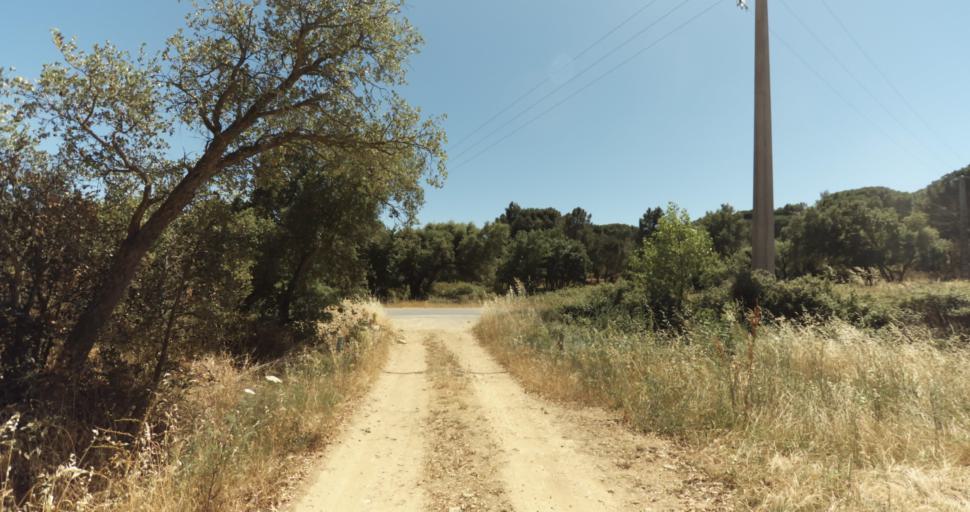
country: FR
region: Provence-Alpes-Cote d'Azur
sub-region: Departement du Var
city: Gassin
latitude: 43.2395
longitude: 6.5672
